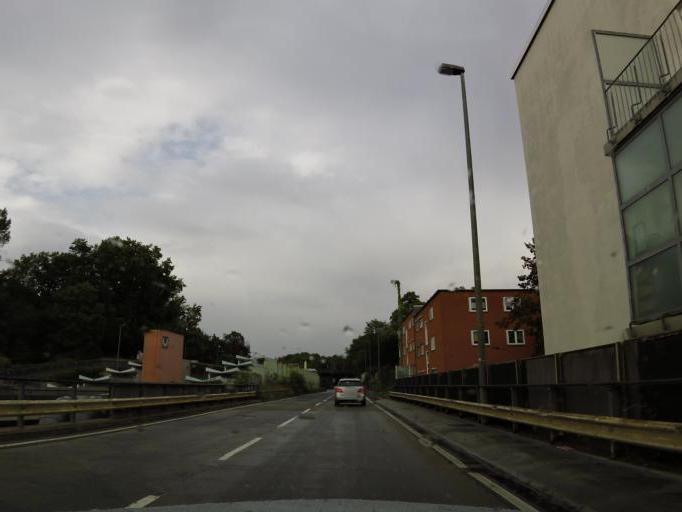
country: DE
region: Hesse
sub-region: Regierungsbezirk Darmstadt
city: Frankfurt am Main
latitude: 50.1520
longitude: 8.6382
